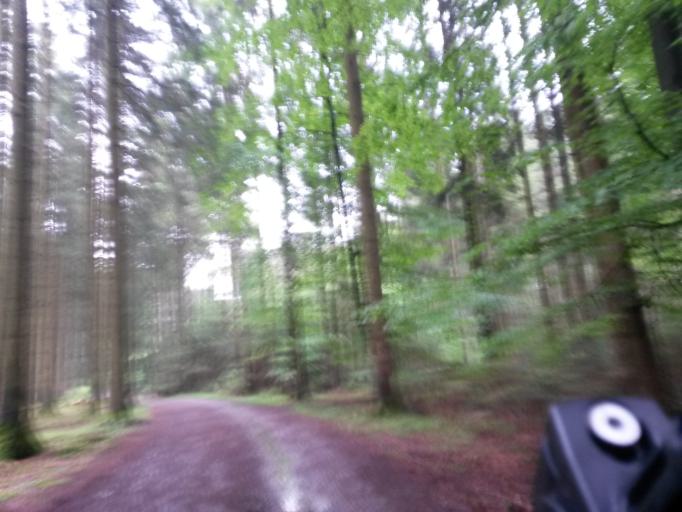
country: DE
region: Baden-Wuerttemberg
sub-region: Tuebingen Region
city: Bad Wurzach
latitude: 47.9230
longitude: 9.8314
